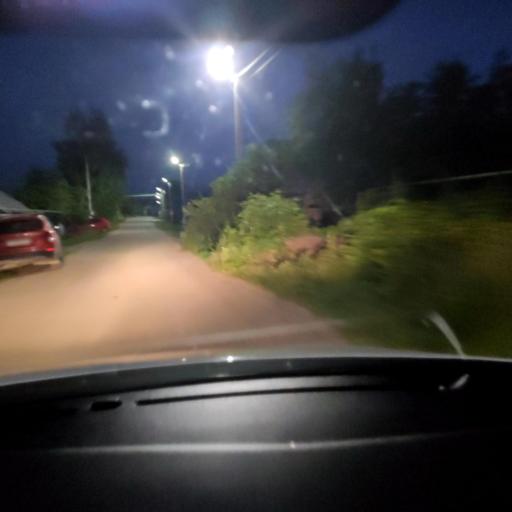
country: RU
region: Tatarstan
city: Staroye Arakchino
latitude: 55.8054
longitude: 48.9511
